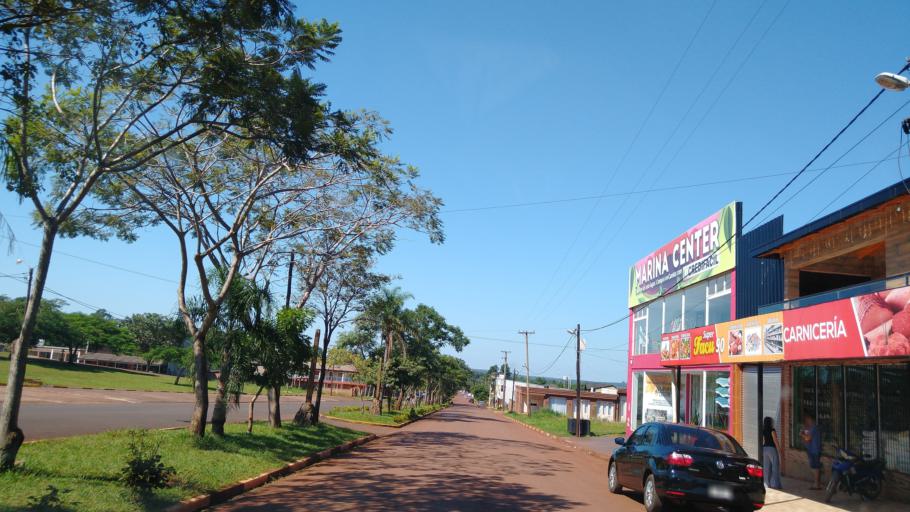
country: AR
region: Misiones
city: Puerto Libertad
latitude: -25.9648
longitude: -54.5605
